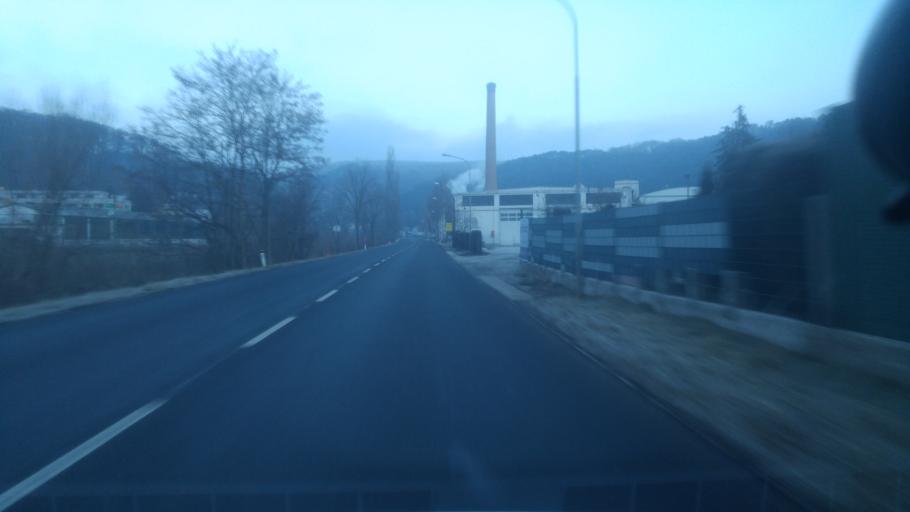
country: AT
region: Lower Austria
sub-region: Politischer Bezirk Baden
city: Pottenstein
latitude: 47.9628
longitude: 16.0896
